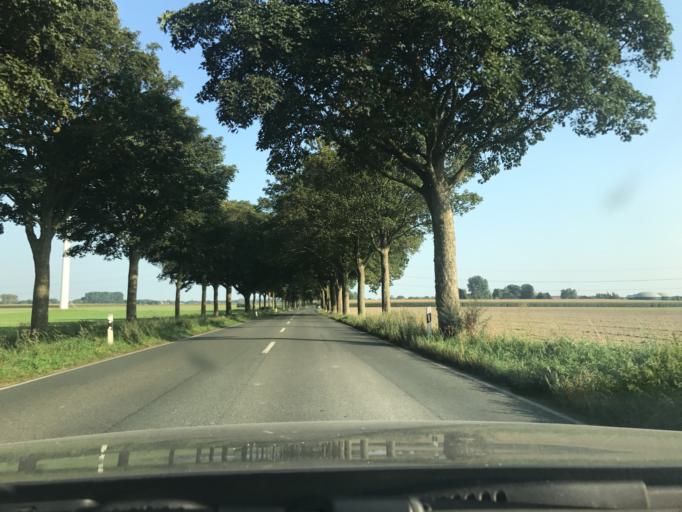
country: DE
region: North Rhine-Westphalia
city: Kalkar
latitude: 51.6964
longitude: 6.2415
